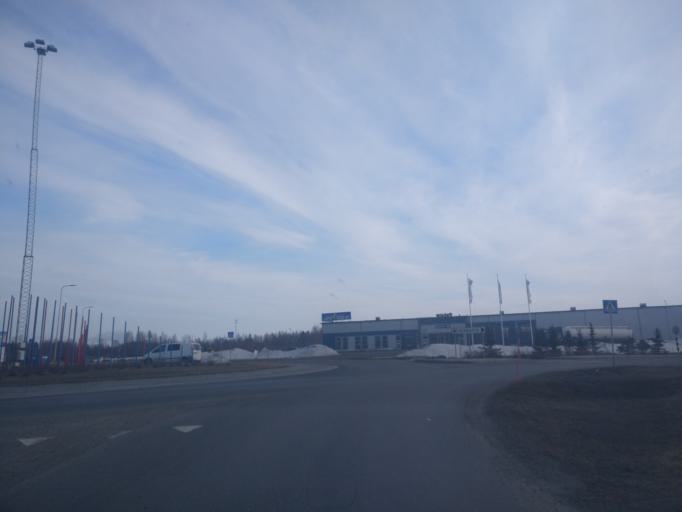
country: FI
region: Lapland
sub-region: Kemi-Tornio
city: Kemi
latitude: 65.7331
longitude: 24.5853
